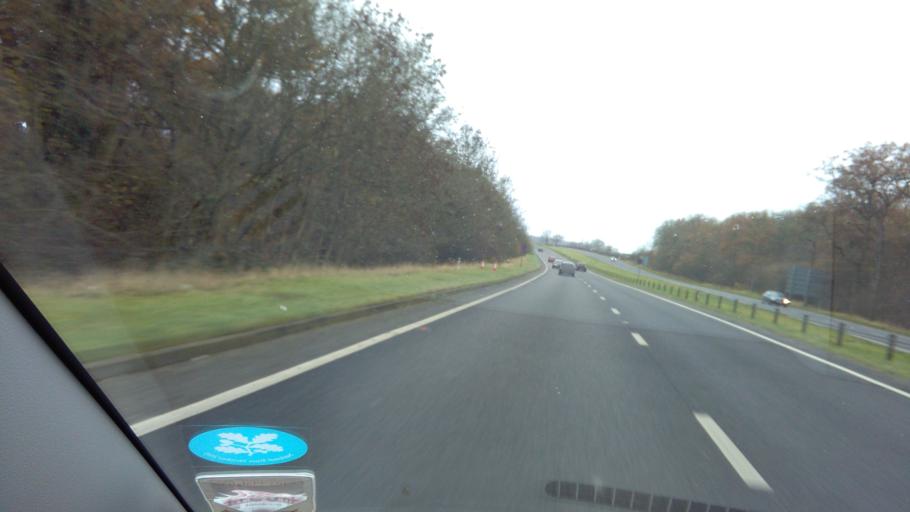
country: GB
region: England
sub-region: Northamptonshire
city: Silverstone
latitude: 52.0769
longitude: -1.0478
